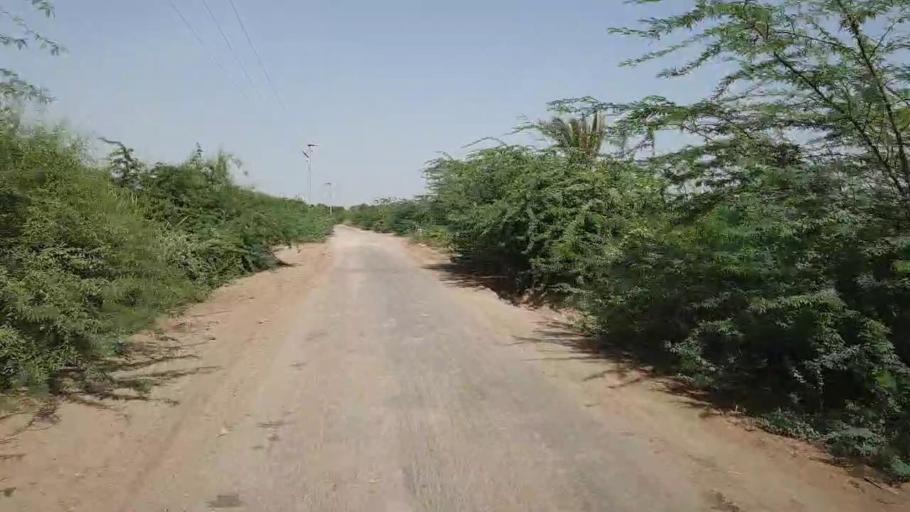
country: PK
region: Sindh
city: Jam Sahib
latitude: 26.4069
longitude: 68.8847
